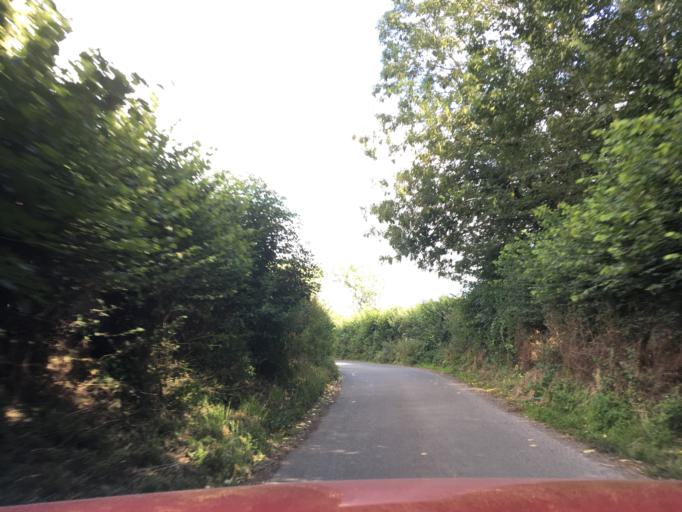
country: GB
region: England
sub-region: Gloucestershire
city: Stonehouse
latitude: 51.8027
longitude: -2.2677
